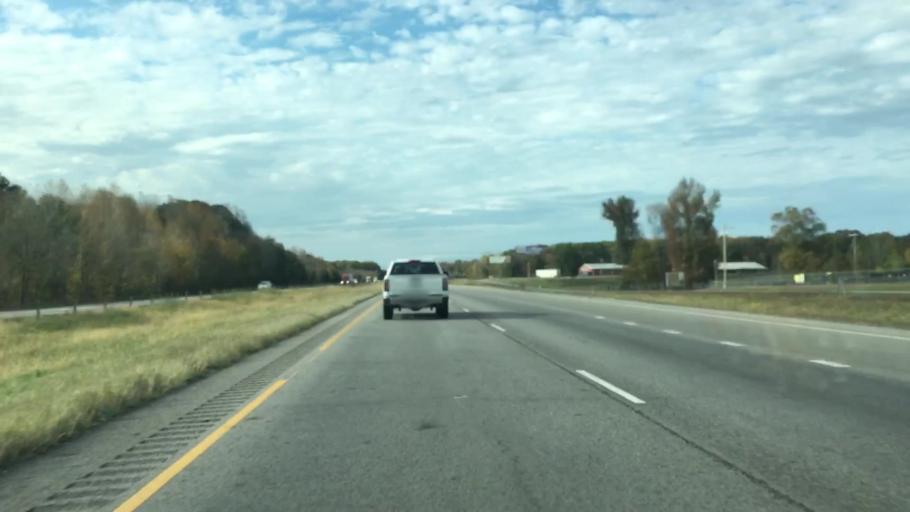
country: US
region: Arkansas
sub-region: Pope County
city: Atkins
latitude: 35.2224
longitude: -92.8339
